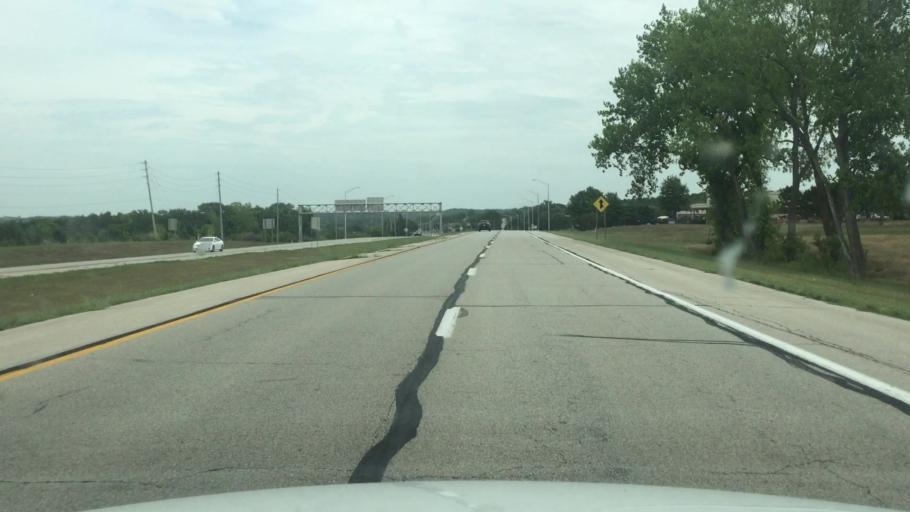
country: US
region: Kansas
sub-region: Wyandotte County
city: Bonner Springs
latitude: 39.0072
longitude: -94.8521
